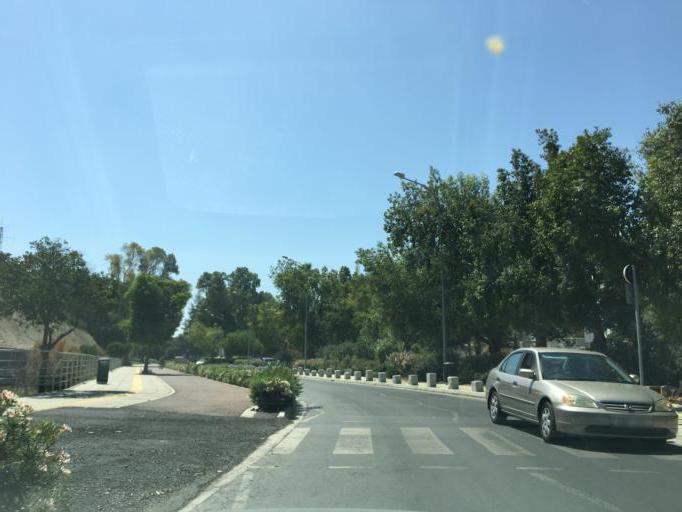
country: CY
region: Lefkosia
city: Nicosia
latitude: 35.1748
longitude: 33.3549
